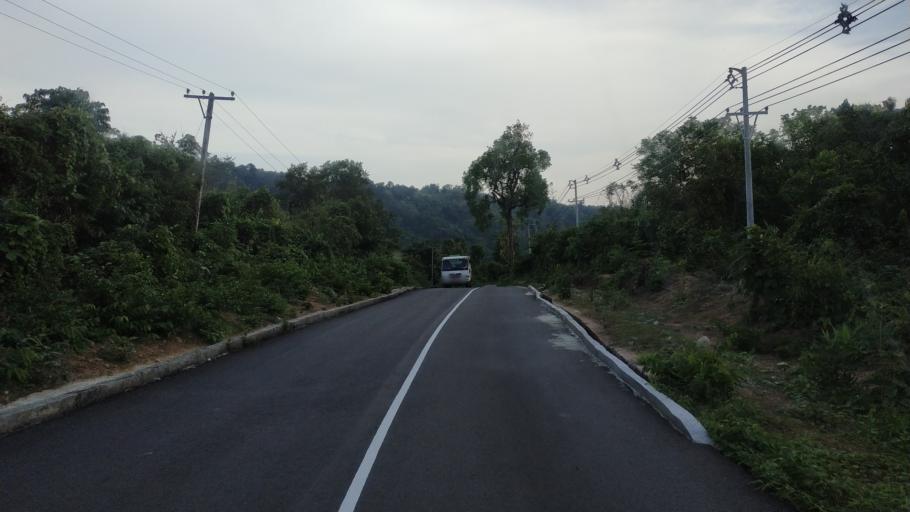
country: MM
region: Mon
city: Kyaikto
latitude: 17.4376
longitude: 97.0962
